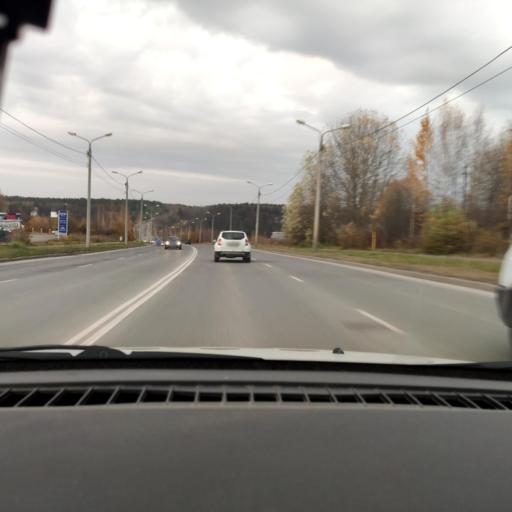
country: RU
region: Perm
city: Perm
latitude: 58.0660
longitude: 56.3653
